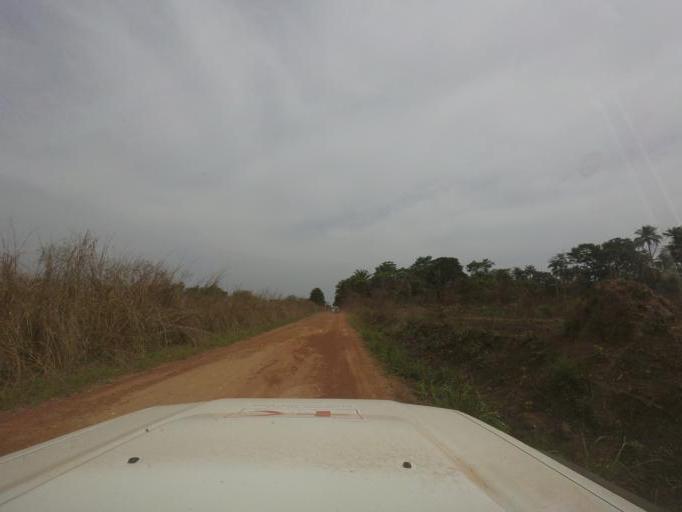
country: GN
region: Nzerekore
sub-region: Prefecture de Guekedou
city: Gueckedou
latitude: 8.4345
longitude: -10.2417
